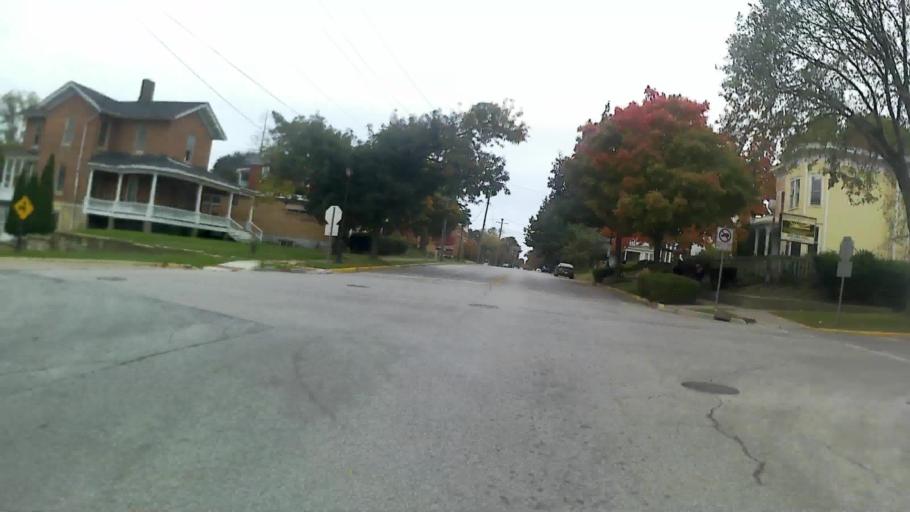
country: US
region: Illinois
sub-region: Kane County
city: Aurora
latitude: 41.7593
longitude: -88.3215
